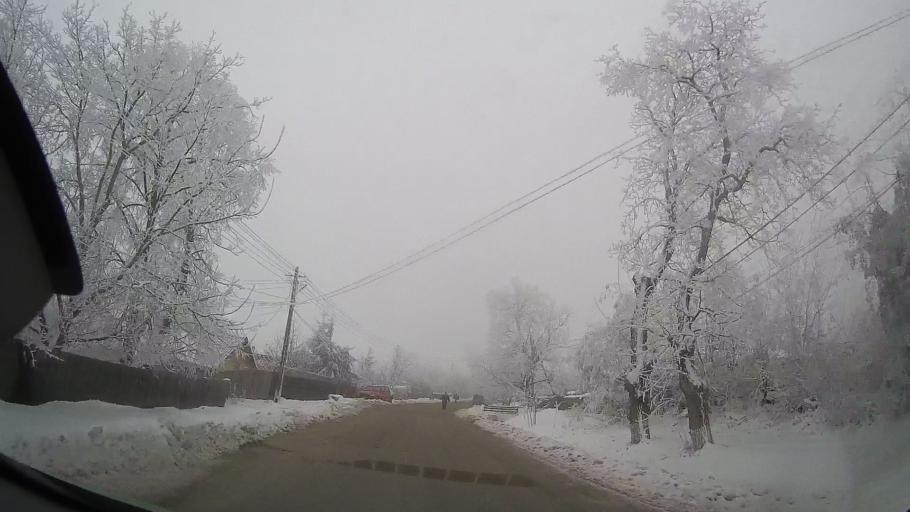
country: RO
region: Neamt
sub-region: Comuna Valea Ursului
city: Valea Ursului
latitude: 46.7975
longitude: 27.0809
